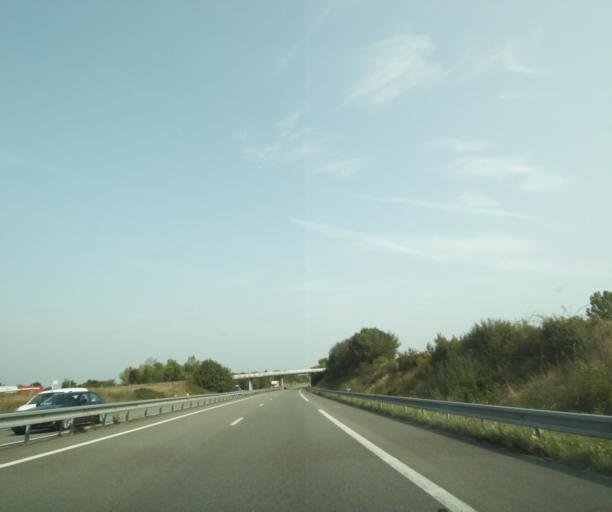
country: FR
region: Pays de la Loire
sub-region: Departement de la Sarthe
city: La Bazoge
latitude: 48.1230
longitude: 0.1456
